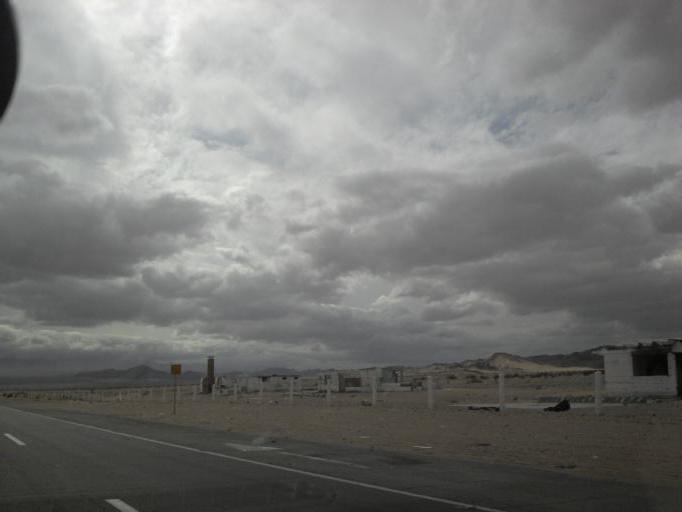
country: MX
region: Baja California
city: Progreso
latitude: 32.5765
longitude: -115.7439
